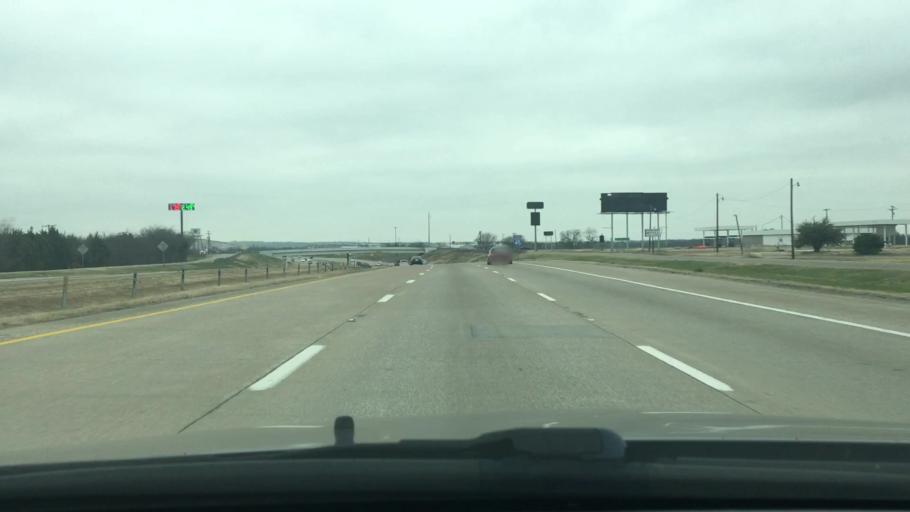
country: US
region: Texas
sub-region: Ellis County
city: Palmer
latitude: 32.4200
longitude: -96.6596
